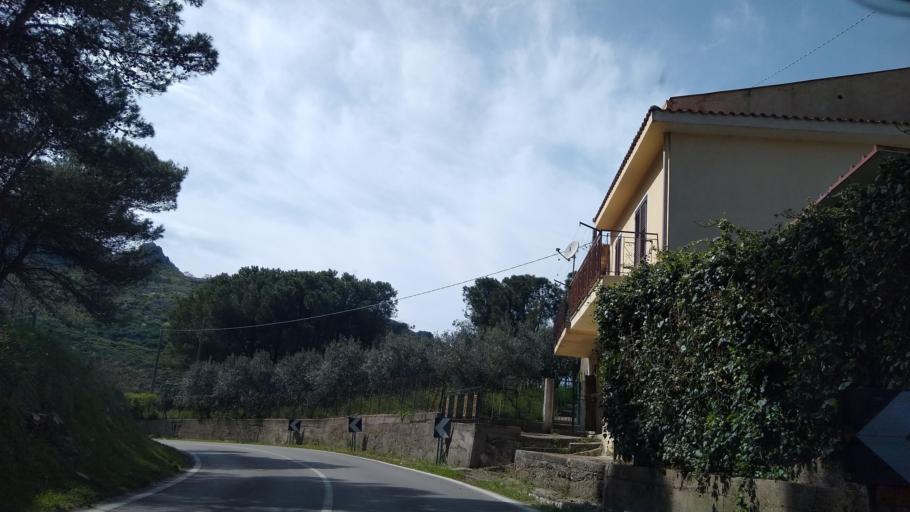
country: IT
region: Sicily
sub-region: Palermo
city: Pioppo
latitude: 38.0415
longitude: 13.2021
